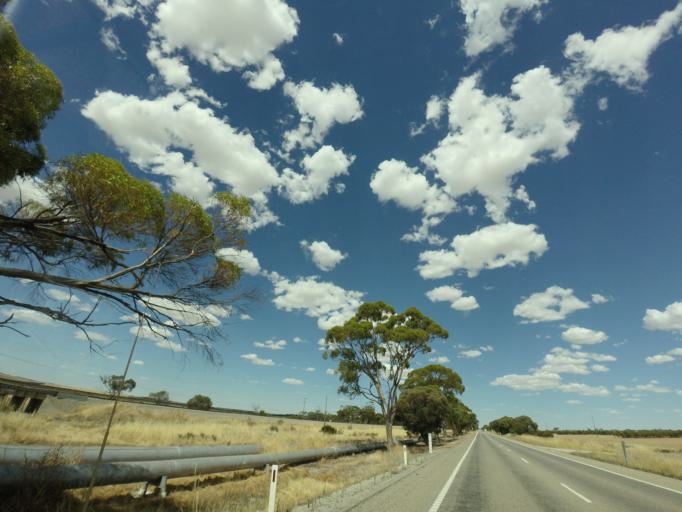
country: AU
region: Western Australia
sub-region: Cunderdin
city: Cunderdin
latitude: -31.6351
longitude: 117.1583
